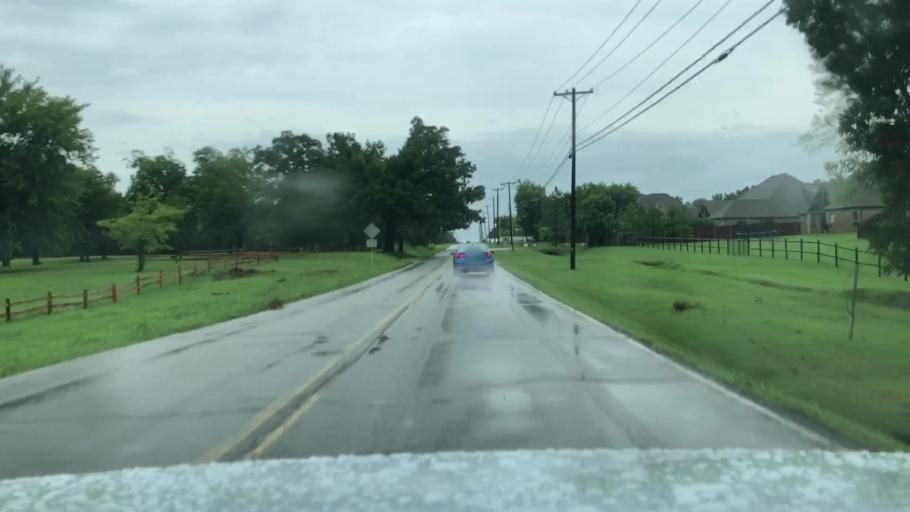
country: US
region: Oklahoma
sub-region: Tulsa County
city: Jenks
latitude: 36.0029
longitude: -95.9961
